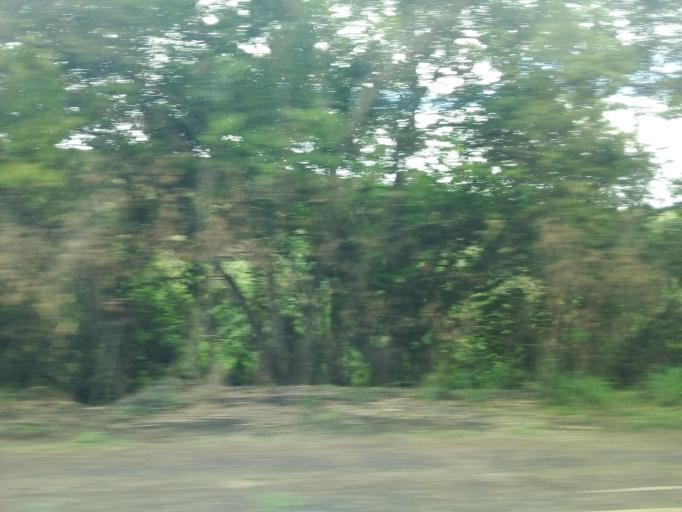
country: BR
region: Minas Gerais
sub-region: Governador Valadares
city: Governador Valadares
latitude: -19.0645
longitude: -42.1494
